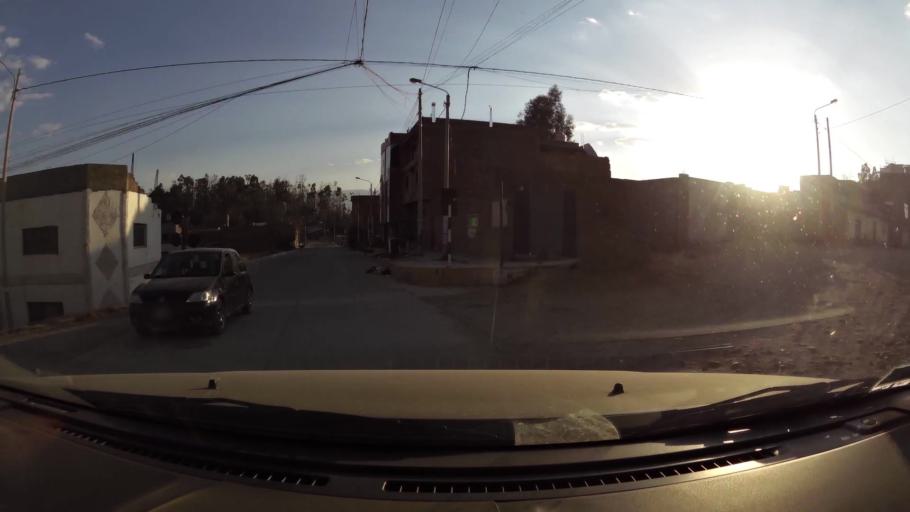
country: PE
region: Junin
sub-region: Provincia de Huancayo
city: Pilcomay
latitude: -12.0323
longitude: -75.2304
